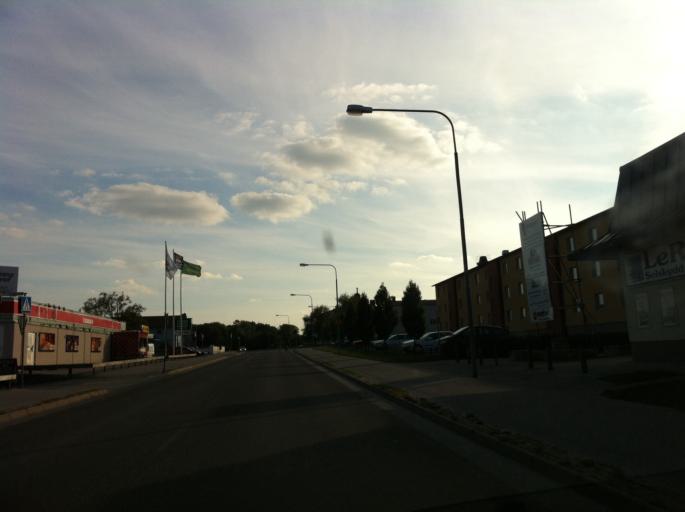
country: SE
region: Gotland
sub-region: Gotland
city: Visby
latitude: 57.6227
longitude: 18.2849
